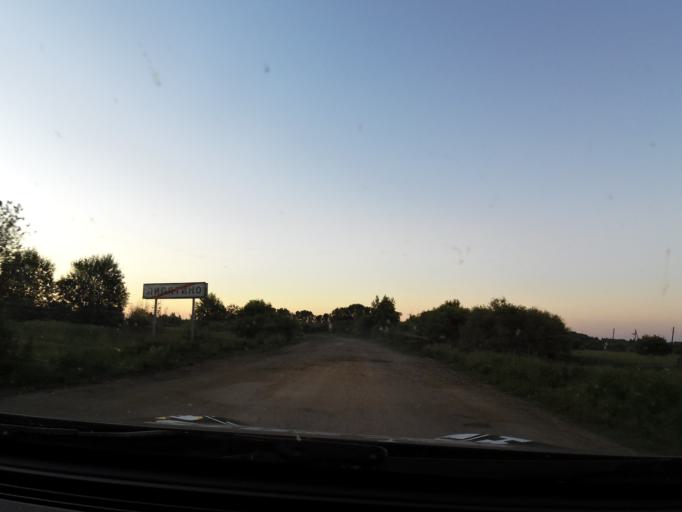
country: RU
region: Kostroma
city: Buy
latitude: 58.4046
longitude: 41.2409
